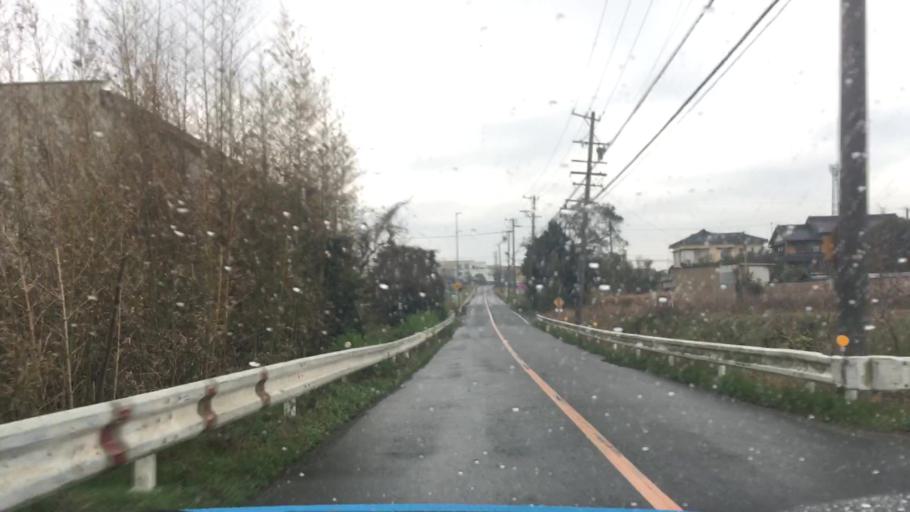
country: JP
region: Aichi
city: Toyohashi
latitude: 34.6856
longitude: 137.3903
